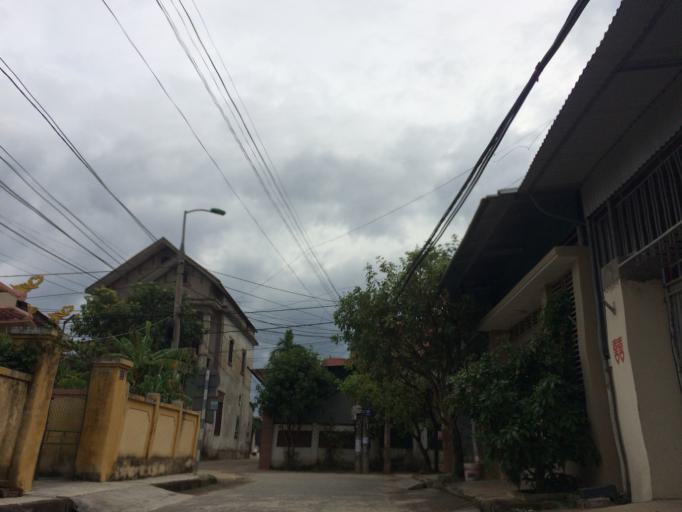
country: VN
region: Ha Tinh
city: Ha Tinh
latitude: 18.3432
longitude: 105.8849
